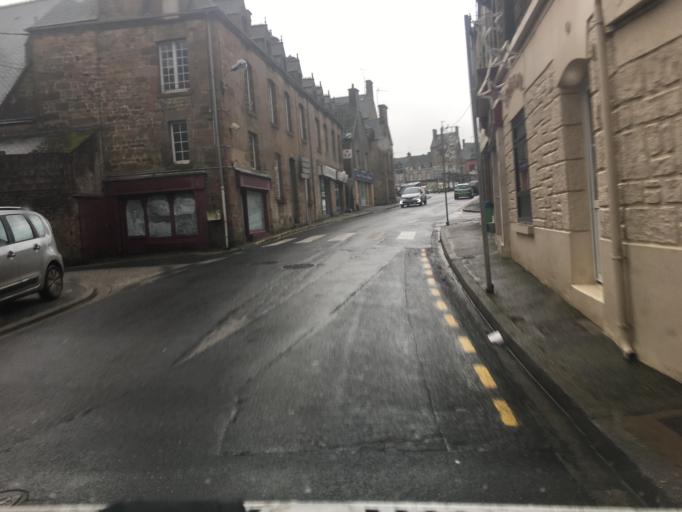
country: FR
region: Lower Normandy
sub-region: Departement de la Manche
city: Saint-Pierre-Eglise
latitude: 49.6693
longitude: -1.4052
